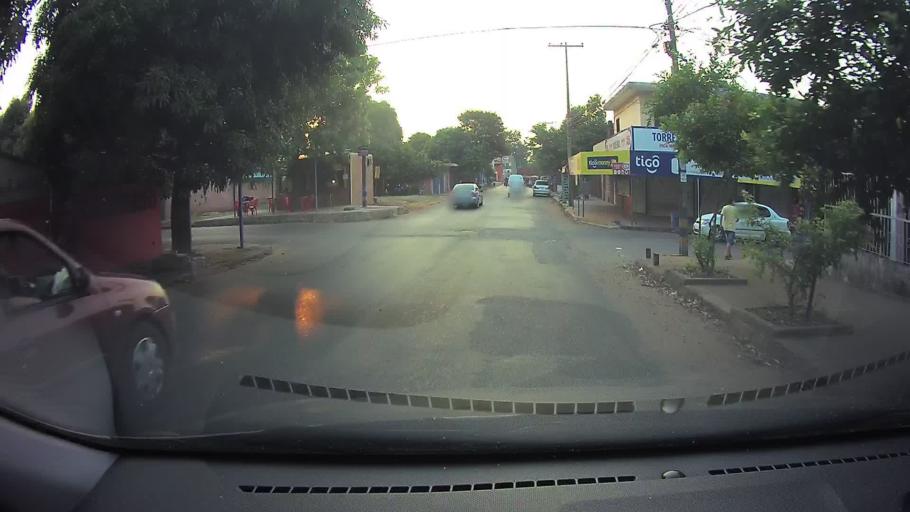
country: PY
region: Central
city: San Lorenzo
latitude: -25.2710
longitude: -57.5007
